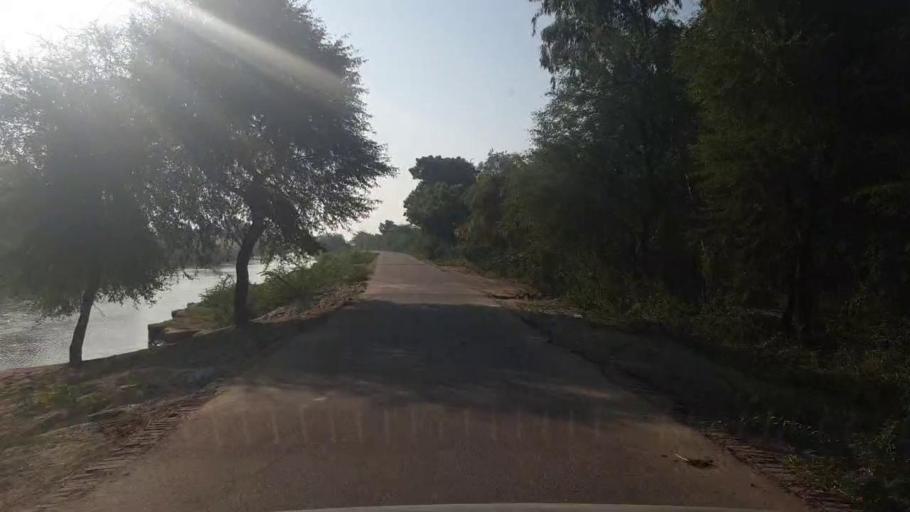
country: PK
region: Sindh
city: Tando Bago
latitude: 24.7257
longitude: 68.9380
